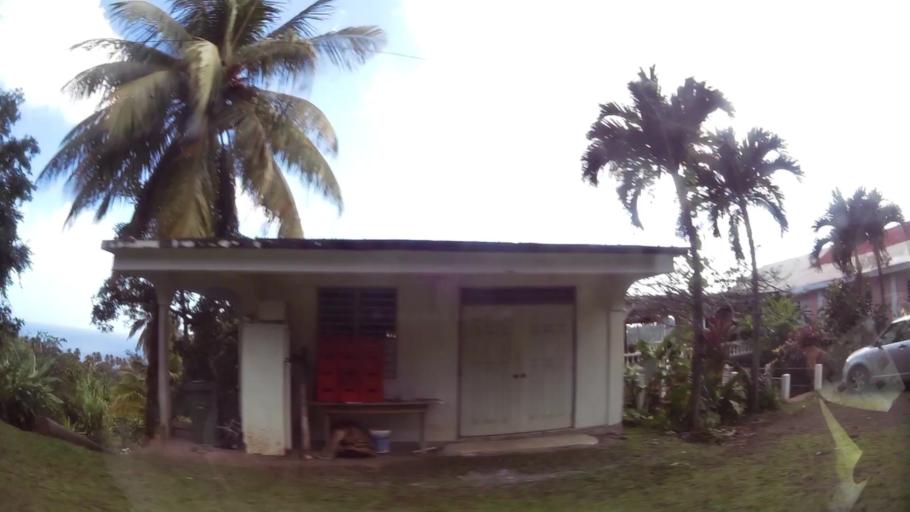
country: DM
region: Saint Andrew
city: Marigot
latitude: 15.5006
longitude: -61.2647
